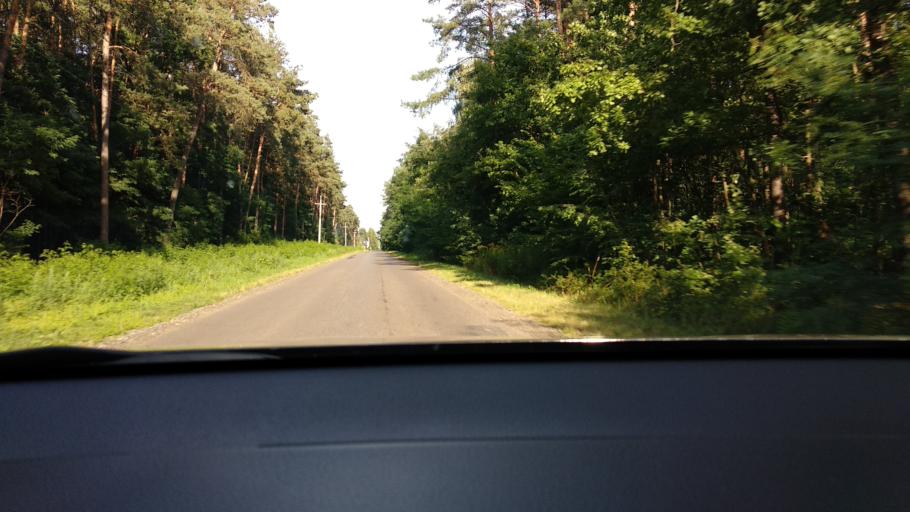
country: PL
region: Masovian Voivodeship
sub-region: Powiat pultuski
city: Pultusk
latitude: 52.7132
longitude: 21.1652
